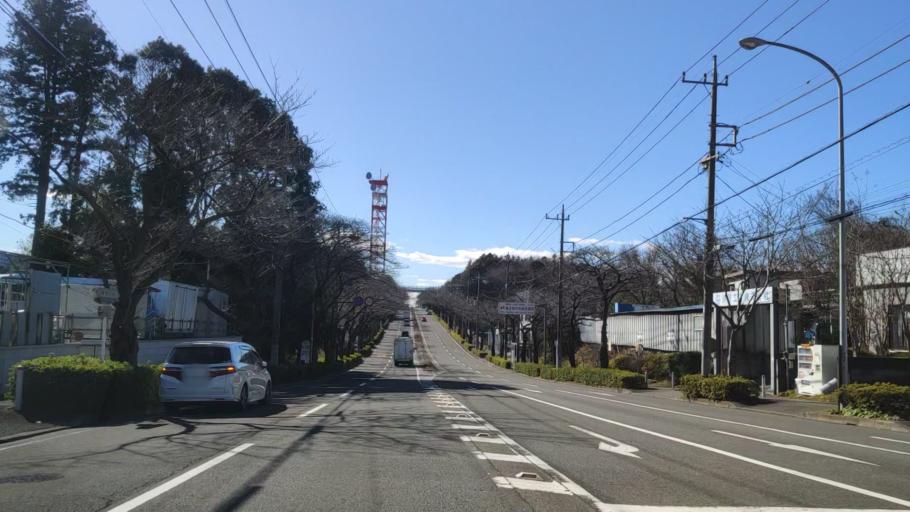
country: JP
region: Tokyo
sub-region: Machida-shi
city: Machida
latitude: 35.5128
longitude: 139.4969
